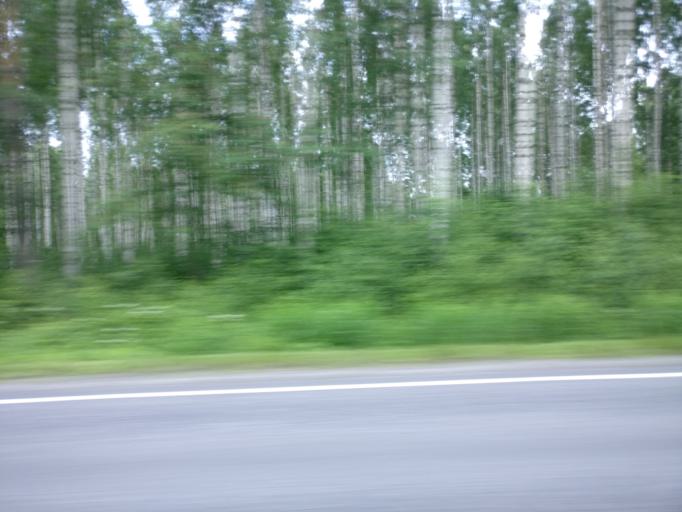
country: FI
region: Southern Savonia
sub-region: Savonlinna
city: Savonlinna
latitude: 61.9153
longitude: 28.9189
